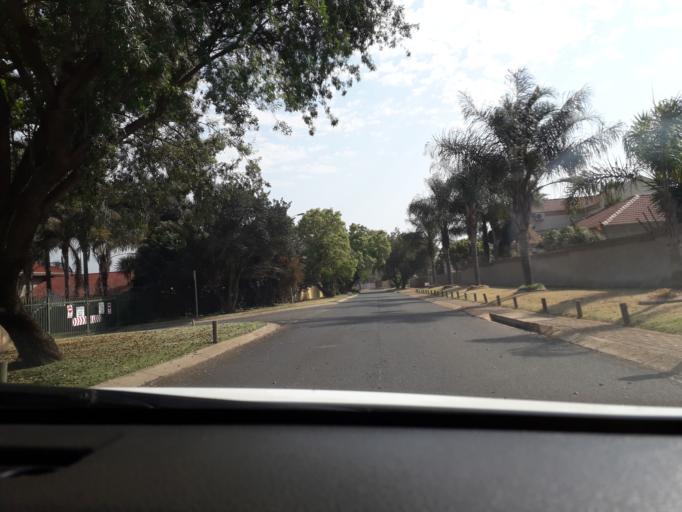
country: ZA
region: Gauteng
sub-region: City of Johannesburg Metropolitan Municipality
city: Modderfontein
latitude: -26.0747
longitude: 28.2409
